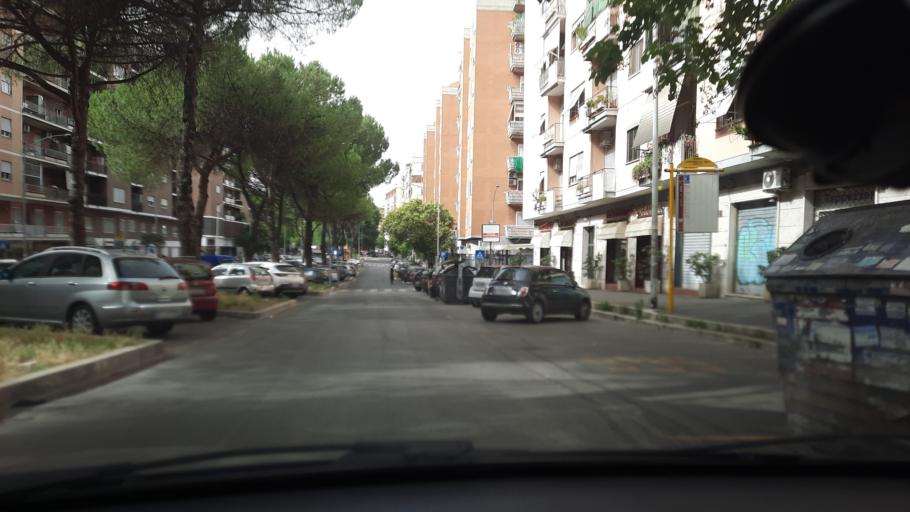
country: IT
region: Latium
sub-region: Citta metropolitana di Roma Capitale
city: Rome
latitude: 41.8549
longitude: 12.4806
